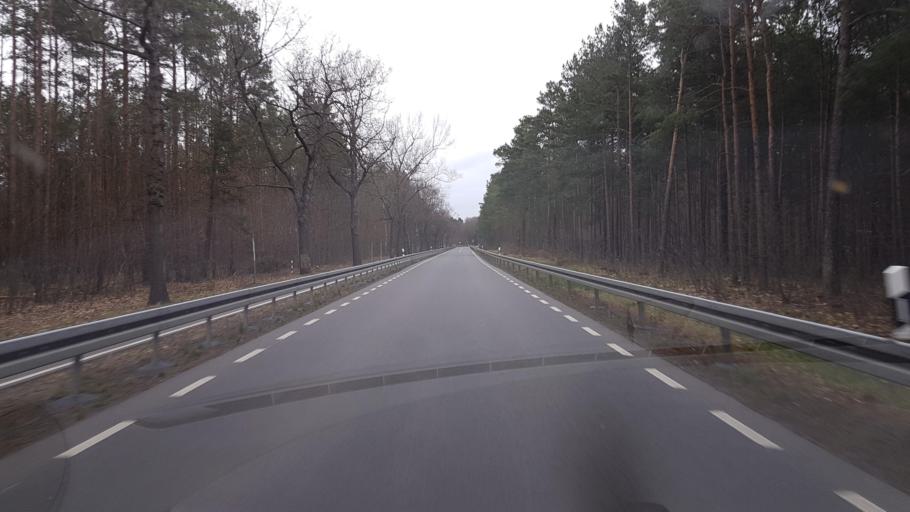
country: DE
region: Saxony
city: Wittichenau
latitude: 51.4041
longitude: 14.3071
